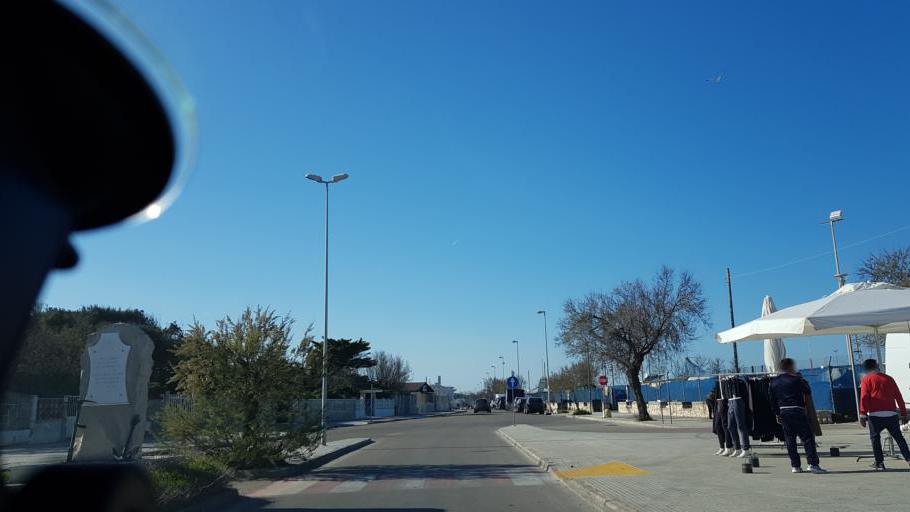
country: IT
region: Apulia
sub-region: Provincia di Brindisi
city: Torchiarolo
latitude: 40.4976
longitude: 18.1219
